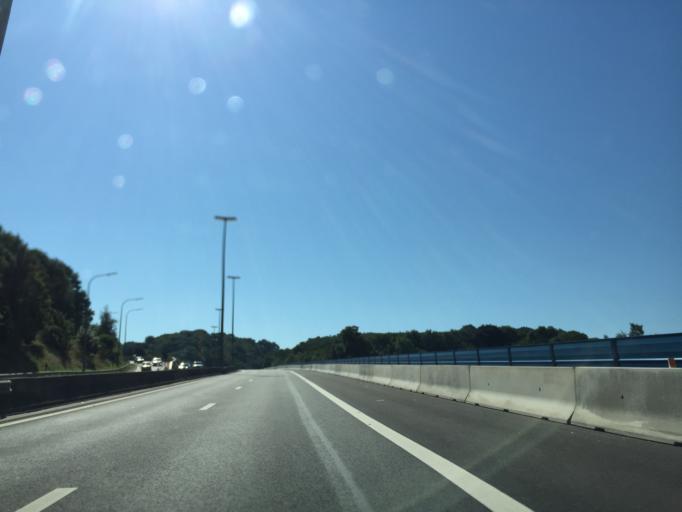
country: BE
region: Wallonia
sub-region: Province de Liege
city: Verviers
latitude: 50.5809
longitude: 5.8504
